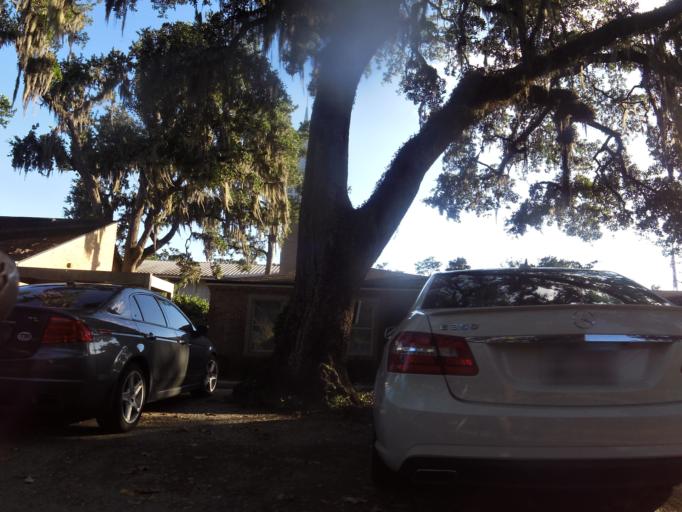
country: US
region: Florida
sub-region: Duval County
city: Jacksonville
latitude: 30.2699
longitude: -81.7110
